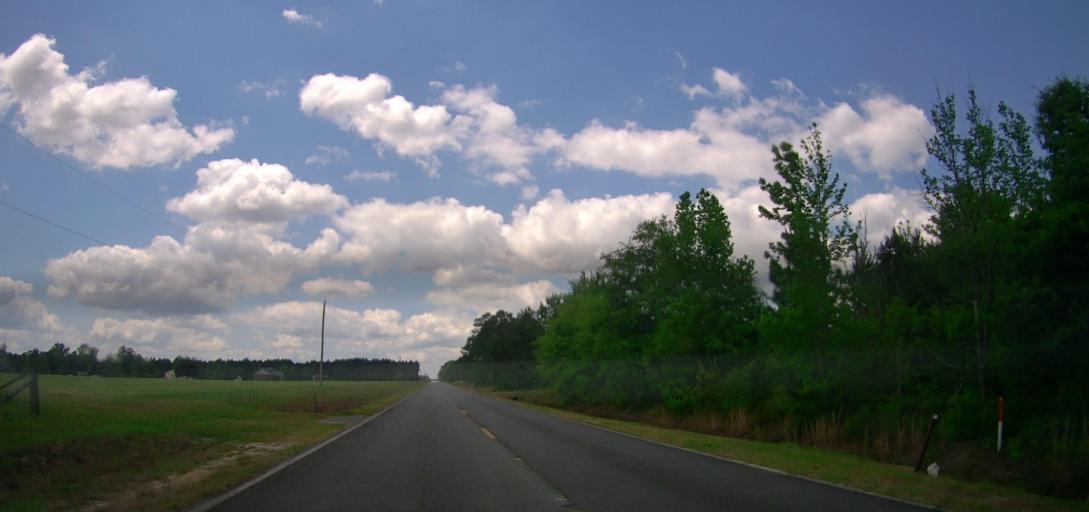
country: US
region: Georgia
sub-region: Treutlen County
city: Soperton
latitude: 32.5249
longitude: -82.6784
